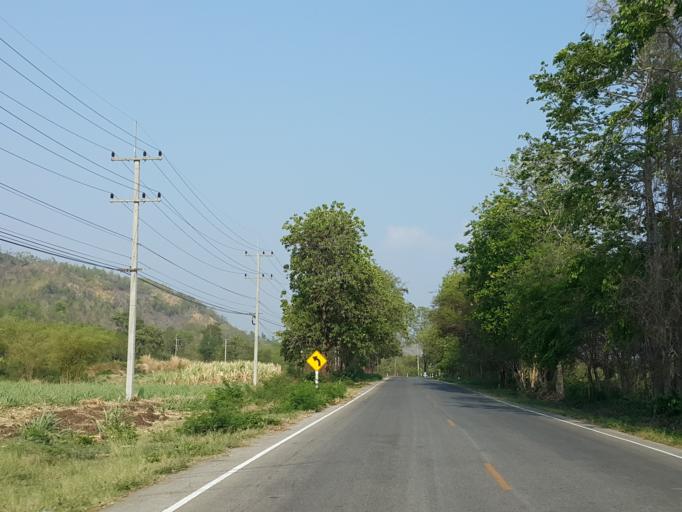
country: TH
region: Kanchanaburi
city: Sai Yok
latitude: 14.2202
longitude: 99.1677
